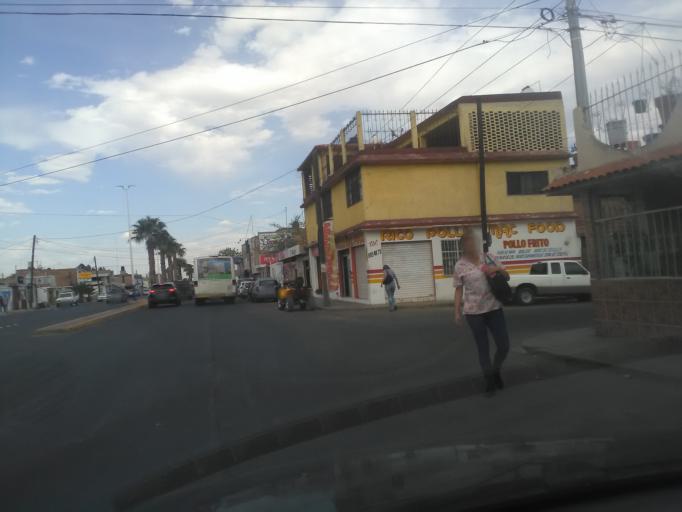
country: MX
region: Durango
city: Victoria de Durango
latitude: 24.0198
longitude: -104.6434
